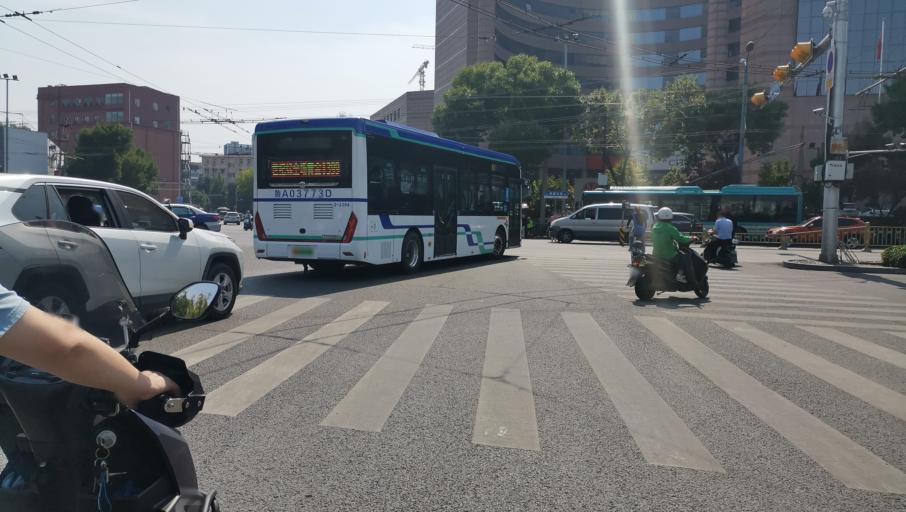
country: CN
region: Shandong Sheng
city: Jinan
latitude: 36.6599
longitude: 117.0125
